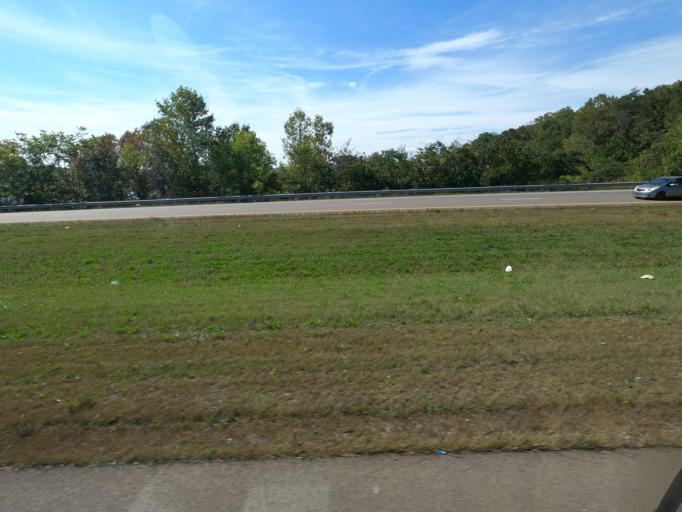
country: US
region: Tennessee
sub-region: Grainger County
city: Bean Station
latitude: 36.2917
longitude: -83.2840
